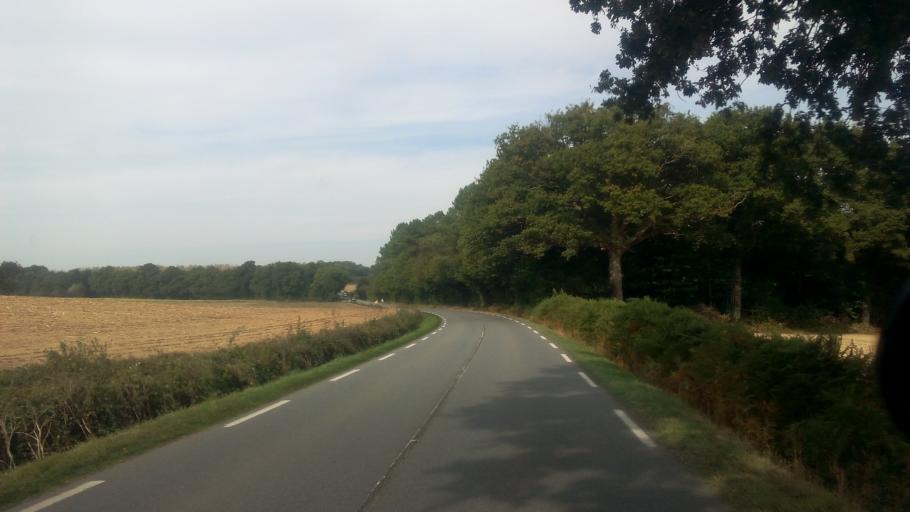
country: FR
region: Brittany
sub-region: Departement d'Ille-et-Vilaine
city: Bains-sur-Oust
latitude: 47.7156
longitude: -2.0917
